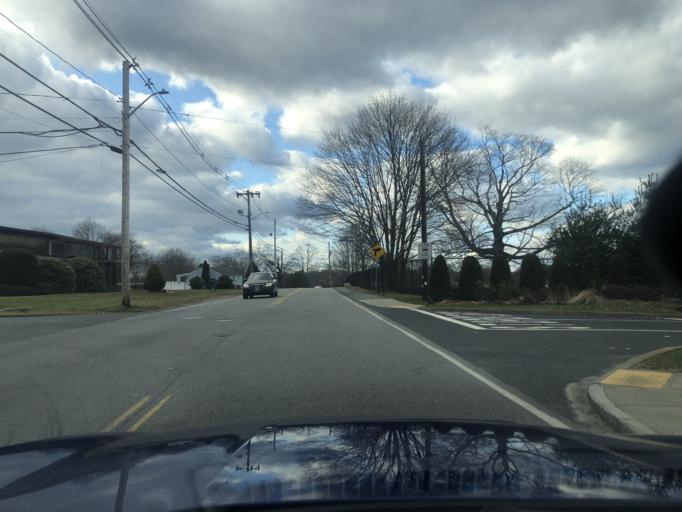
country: US
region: Massachusetts
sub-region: Plymouth County
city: Brockton
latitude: 42.0980
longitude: -71.0326
